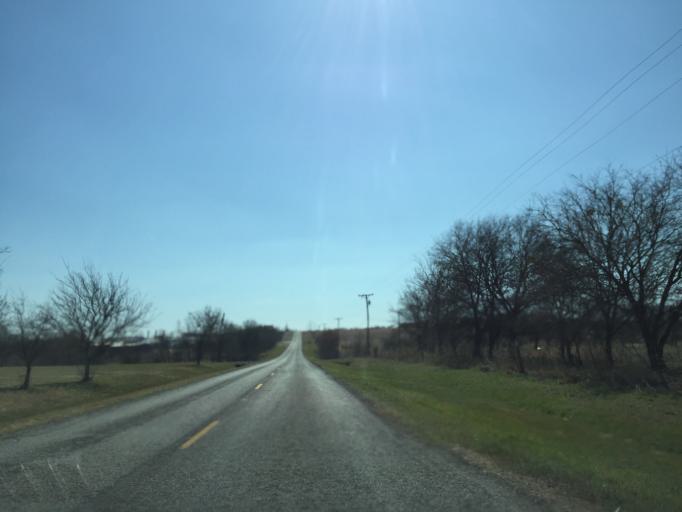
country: US
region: Texas
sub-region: Williamson County
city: Serenada
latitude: 30.7283
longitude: -97.5847
